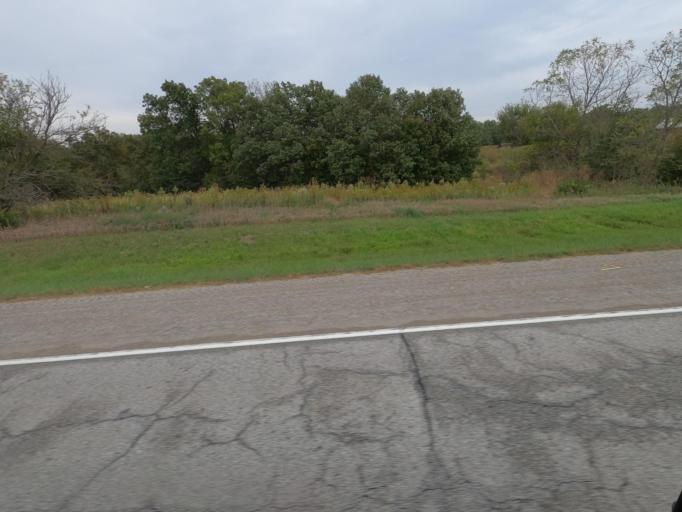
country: US
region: Iowa
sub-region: Van Buren County
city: Keosauqua
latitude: 40.8399
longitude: -92.0094
